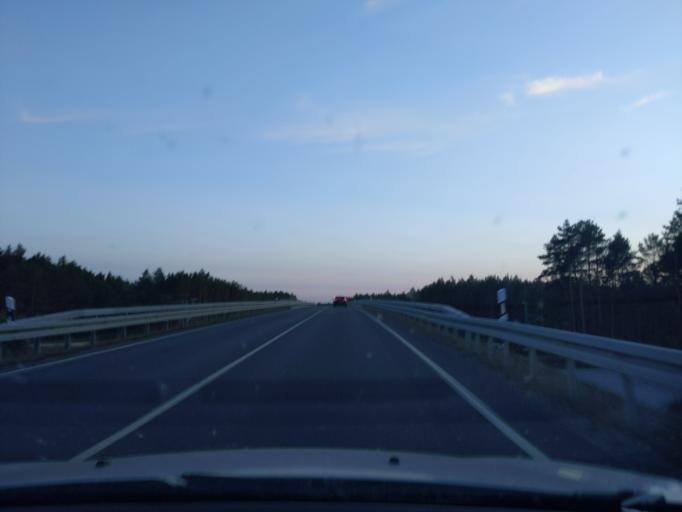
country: DE
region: Saxony
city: Hoyerswerda
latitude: 51.4253
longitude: 14.2980
